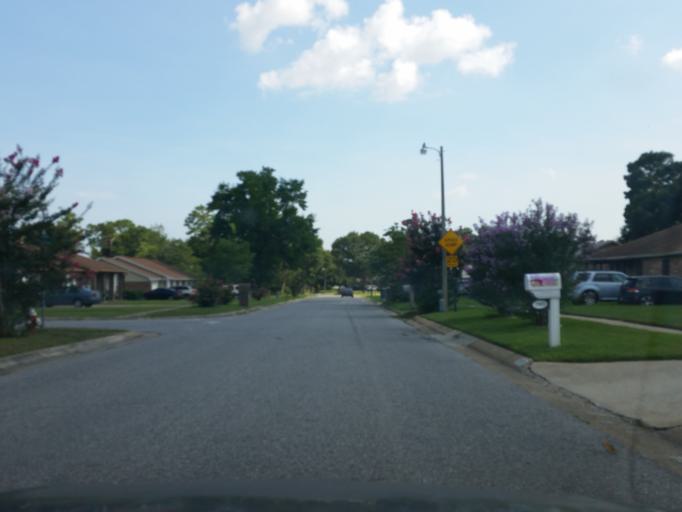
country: US
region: Florida
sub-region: Escambia County
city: Ferry Pass
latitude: 30.5081
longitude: -87.1809
